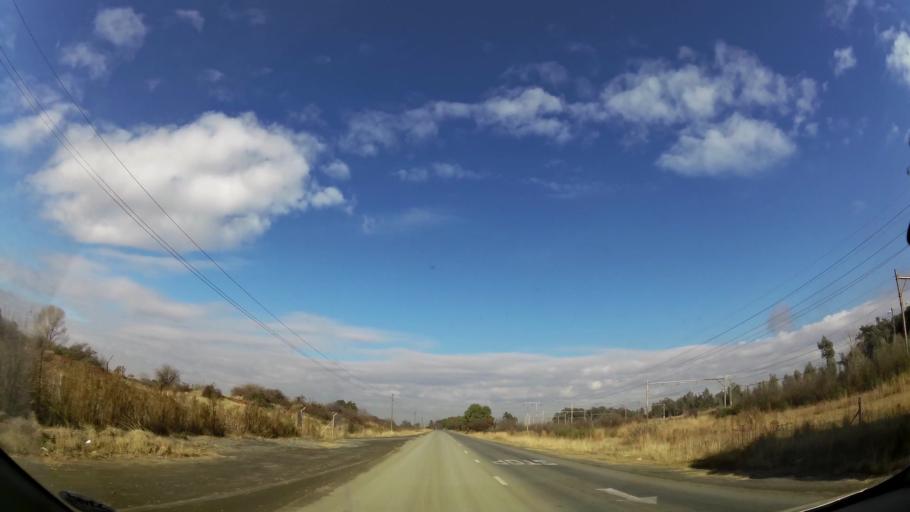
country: ZA
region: Gauteng
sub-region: Sedibeng District Municipality
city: Meyerton
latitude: -26.5134
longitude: 28.0517
